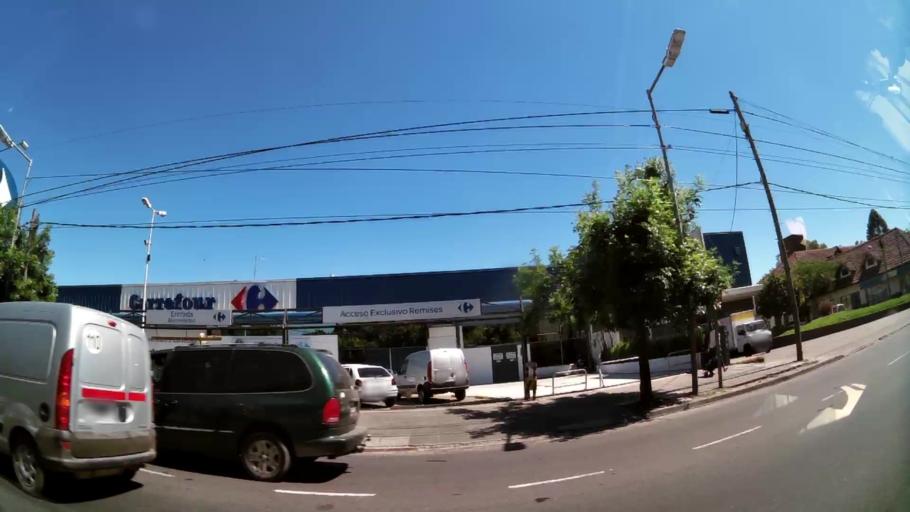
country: AR
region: Buenos Aires
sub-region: Partido de Tigre
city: Tigre
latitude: -34.4917
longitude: -58.6271
